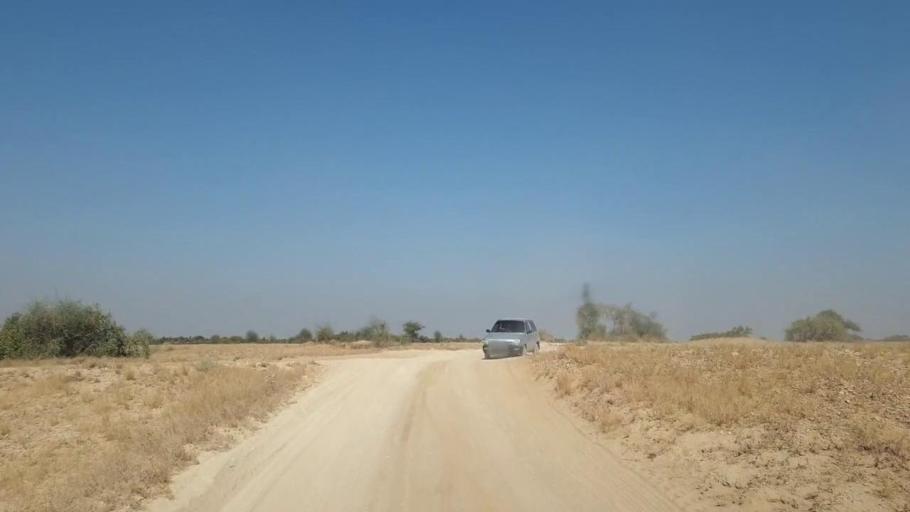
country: PK
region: Sindh
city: Jamshoro
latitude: 25.2789
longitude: 67.8073
